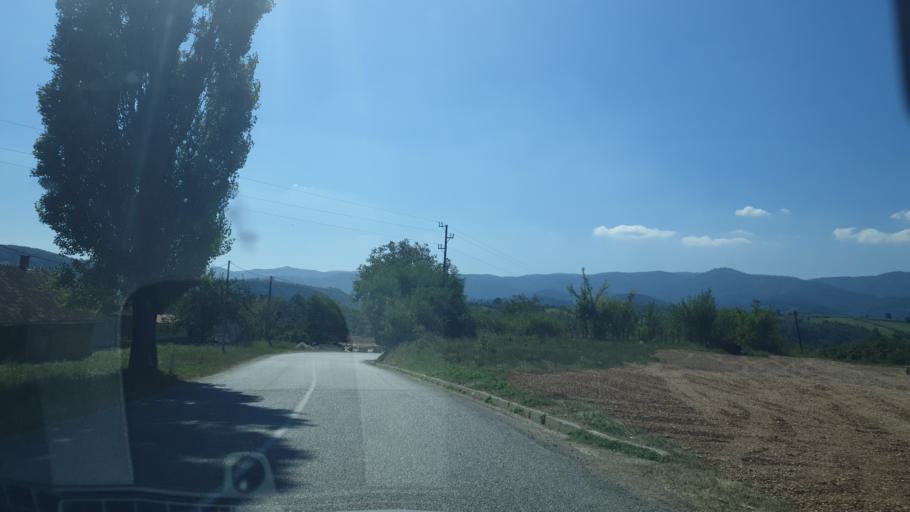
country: RS
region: Central Serbia
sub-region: Kolubarski Okrug
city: Mionica
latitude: 44.1925
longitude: 20.0721
